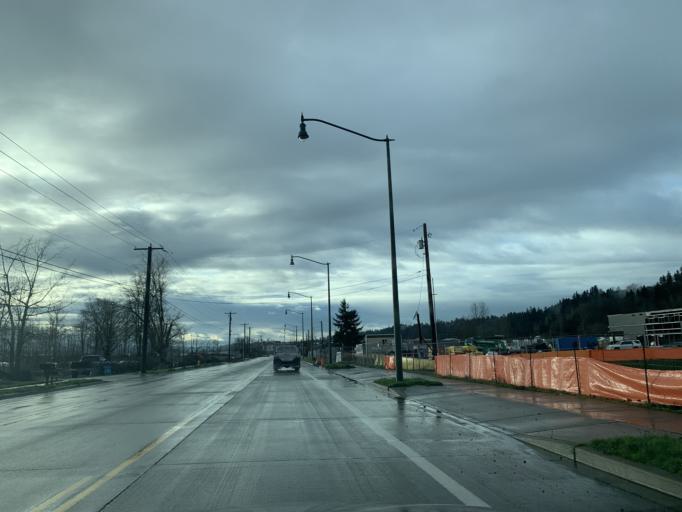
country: US
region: Washington
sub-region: King County
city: Pacific
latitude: 47.2401
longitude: -122.2488
